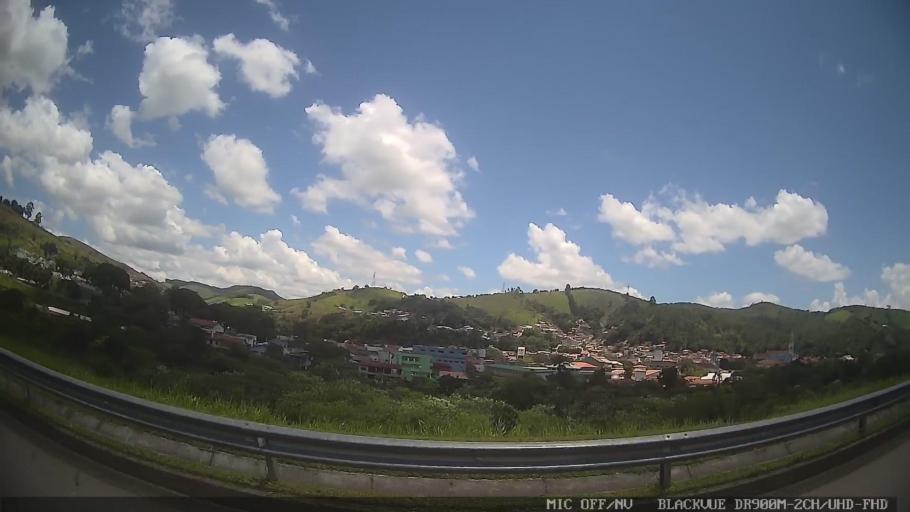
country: BR
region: Sao Paulo
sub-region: Santa Branca
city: Santa Branca
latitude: -23.3883
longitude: -45.6573
